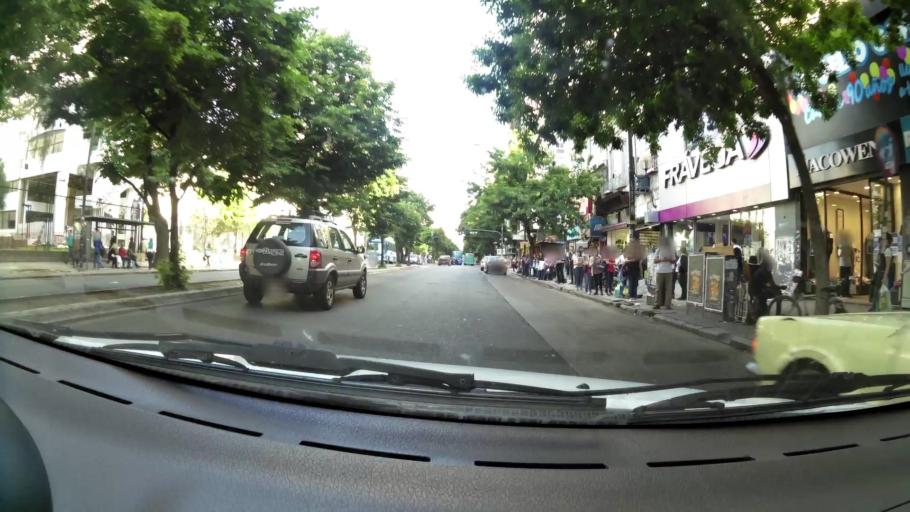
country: AR
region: Buenos Aires
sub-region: Partido de La Plata
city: La Plata
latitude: -34.9134
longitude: -57.9517
